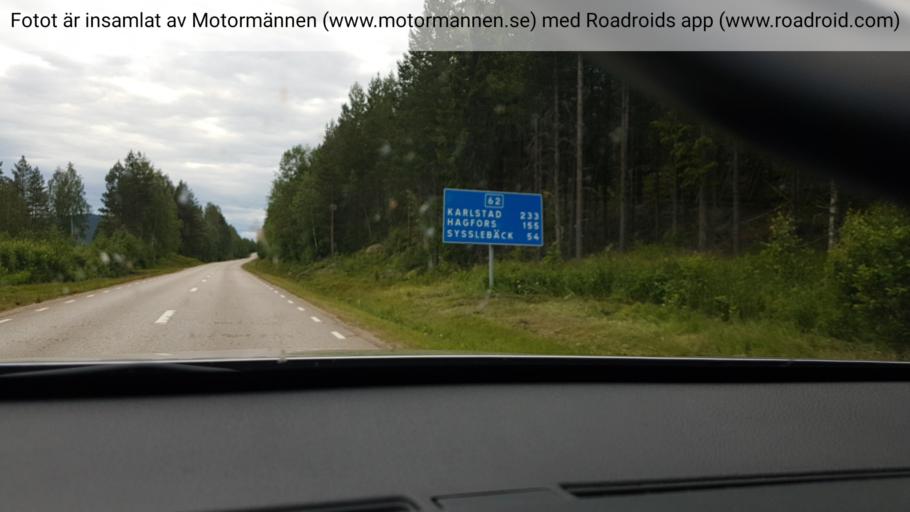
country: NO
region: Hedmark
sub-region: Trysil
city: Innbygda
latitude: 61.0408
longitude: 12.5874
